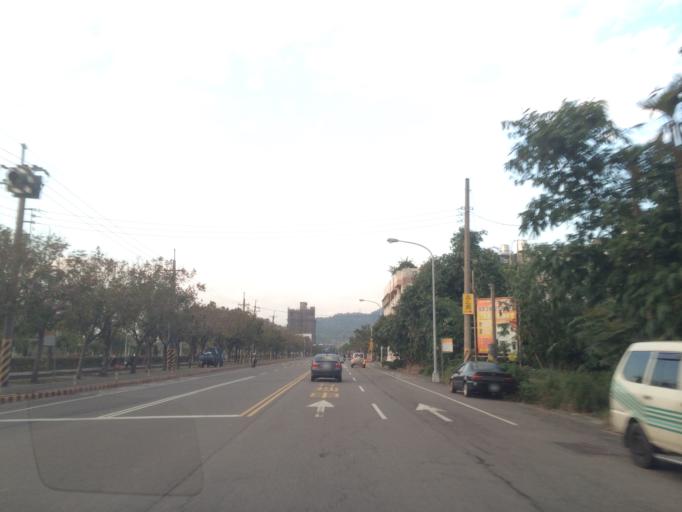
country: TW
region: Taiwan
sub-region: Taichung City
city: Taichung
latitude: 24.1645
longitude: 120.7334
